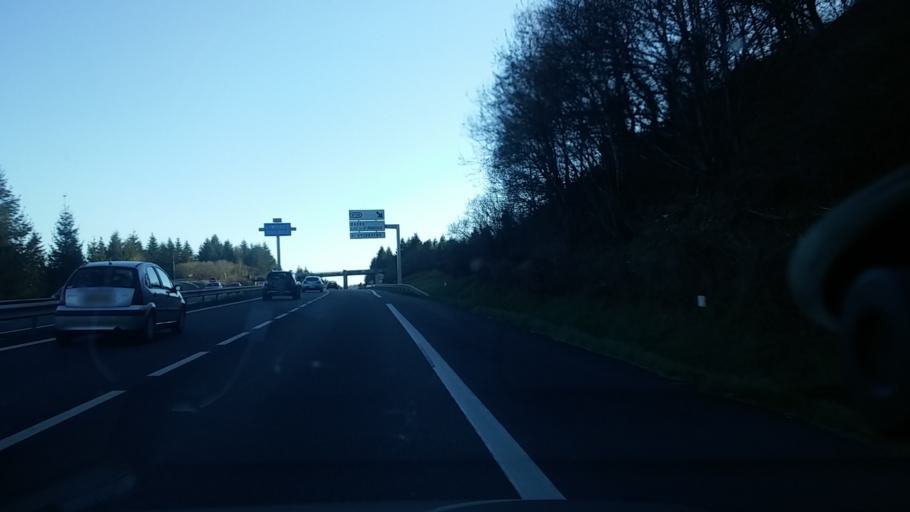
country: FR
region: Limousin
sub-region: Departement de la Haute-Vienne
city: Razes
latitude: 46.0282
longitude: 1.3464
